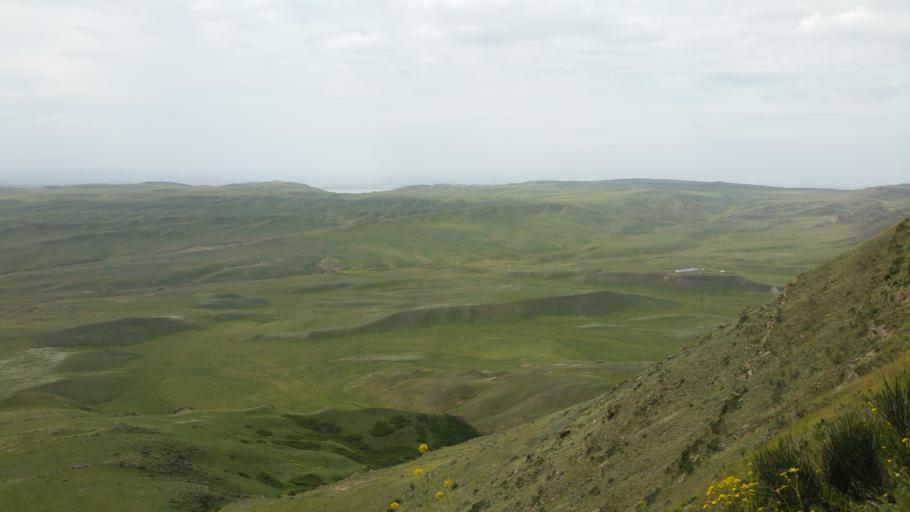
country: AZ
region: Agstafa
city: Saloglu
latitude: 41.4427
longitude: 45.3760
